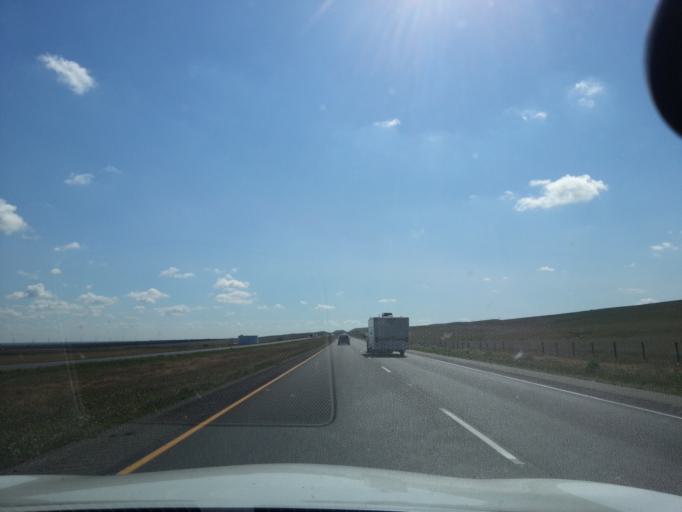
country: US
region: California
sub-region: Fresno County
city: Coalinga
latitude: 36.3446
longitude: -120.3128
